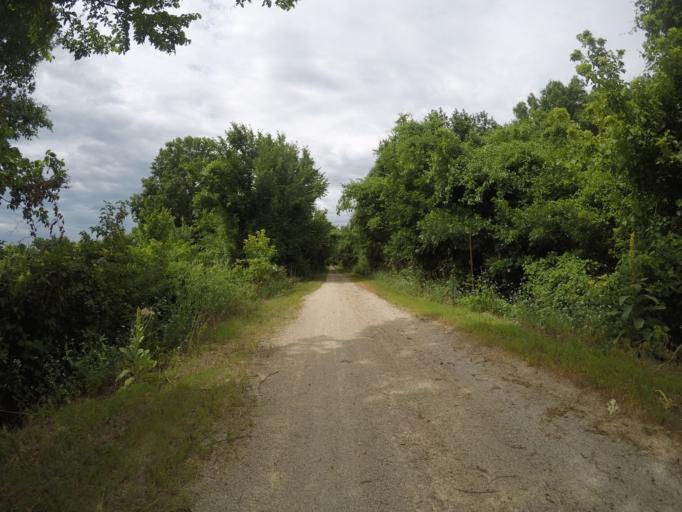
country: US
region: Kansas
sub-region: Anderson County
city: Garnett
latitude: 38.3373
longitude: -95.2418
